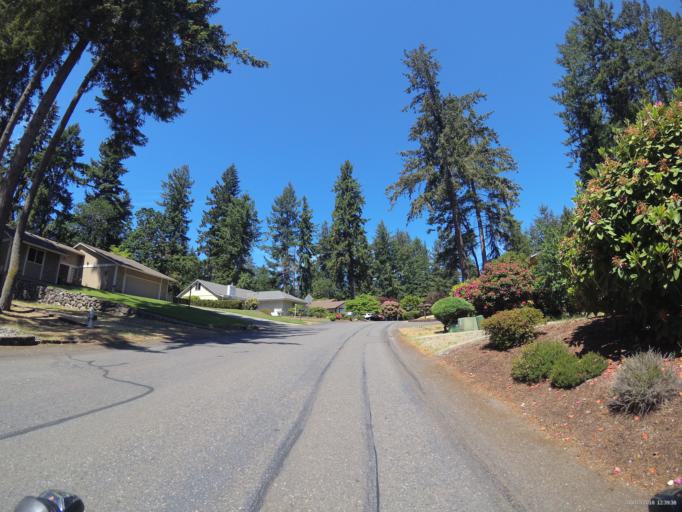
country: US
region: Washington
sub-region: Pierce County
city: University Place
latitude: 47.2005
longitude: -122.5561
